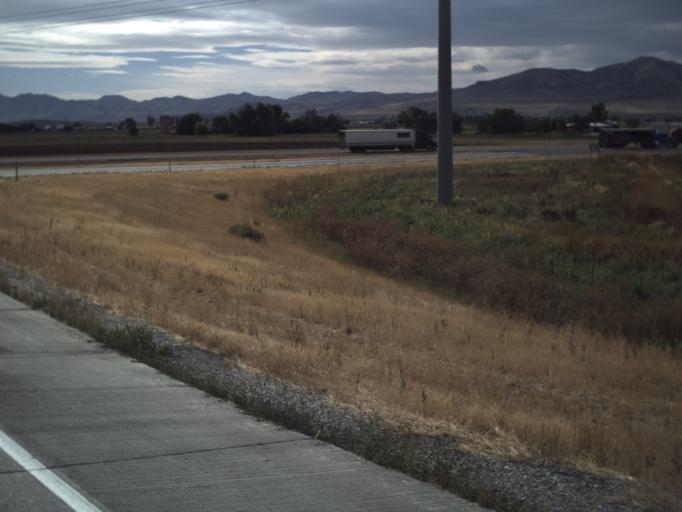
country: US
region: Utah
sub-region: Box Elder County
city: Tremonton
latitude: 41.7074
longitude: -112.1933
